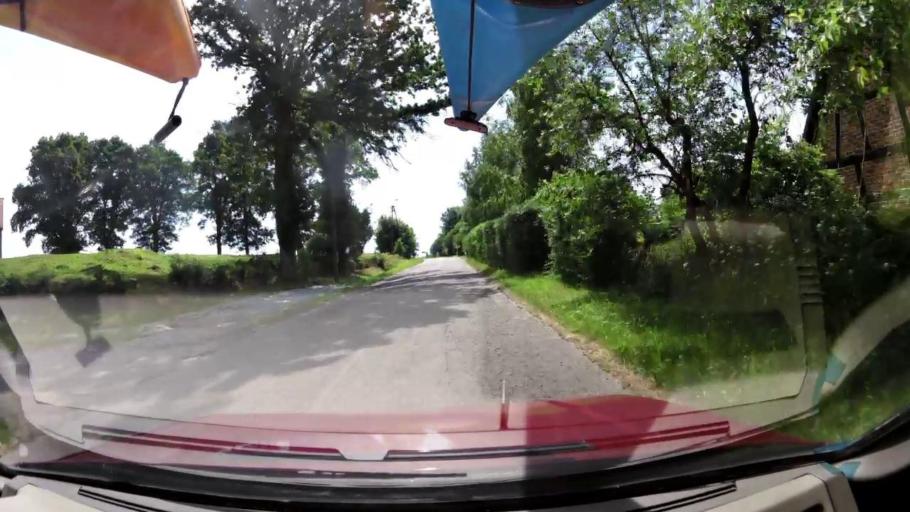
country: PL
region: West Pomeranian Voivodeship
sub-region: Powiat slawienski
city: Darlowo
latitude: 54.3168
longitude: 16.4178
